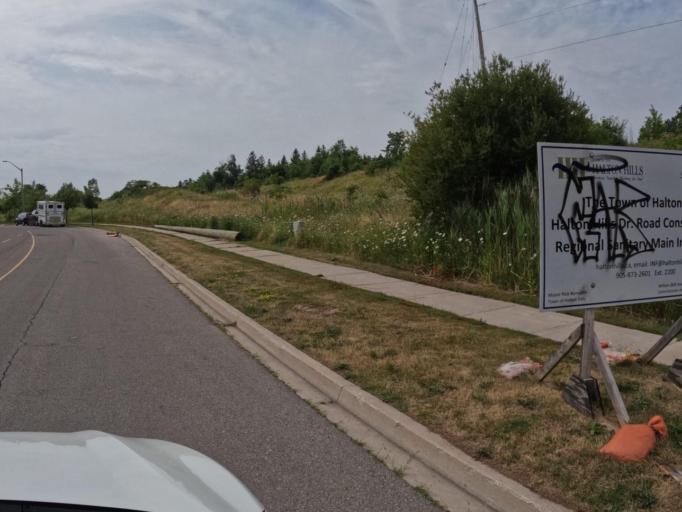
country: CA
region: Ontario
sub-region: Halton
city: Milton
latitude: 43.6429
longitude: -79.9346
